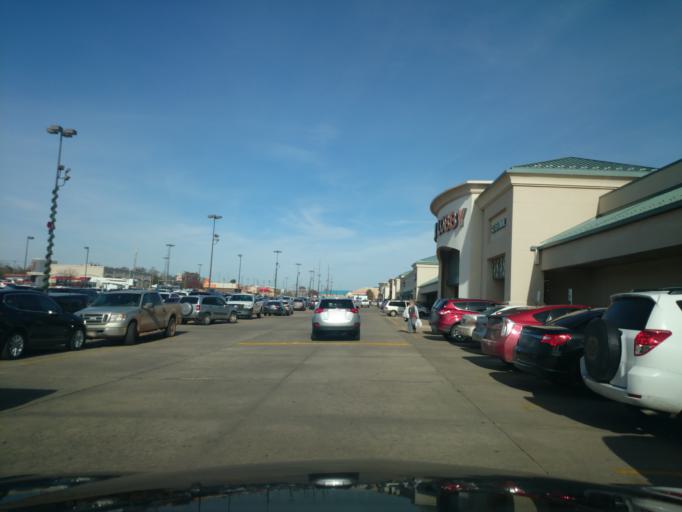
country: US
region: Oklahoma
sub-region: Payne County
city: Stillwater
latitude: 36.1272
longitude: -97.0500
